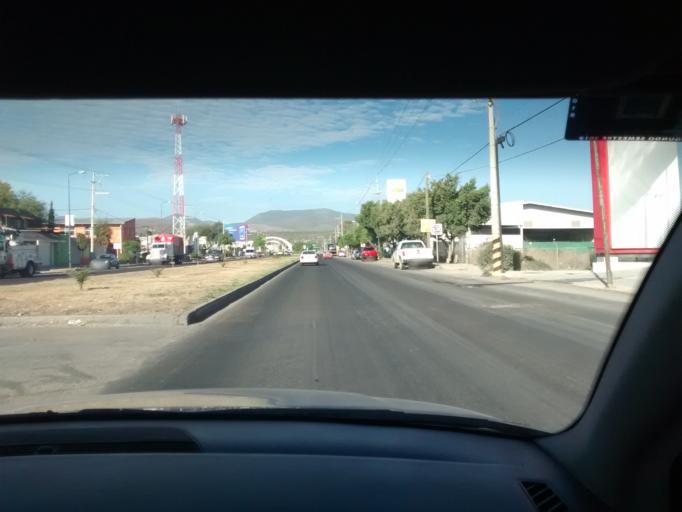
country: MX
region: Puebla
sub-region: Santiago Miahuatlan
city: San Jose Monte Chiquito
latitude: 18.4782
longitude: -97.4226
